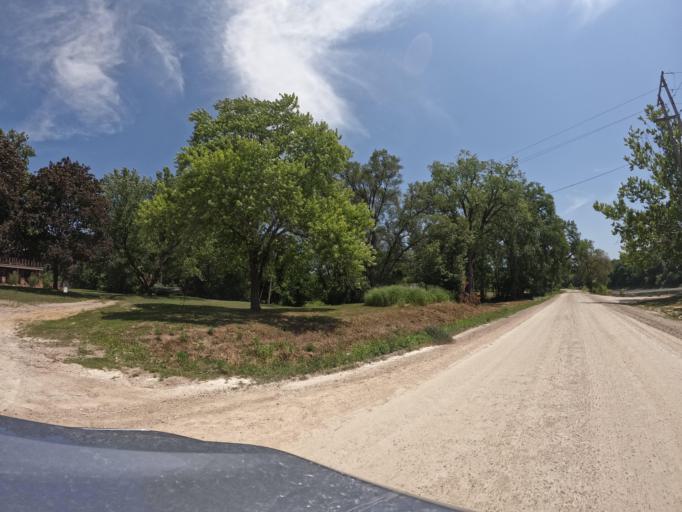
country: US
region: Iowa
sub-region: Henry County
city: Mount Pleasant
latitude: 40.9357
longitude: -91.6153
